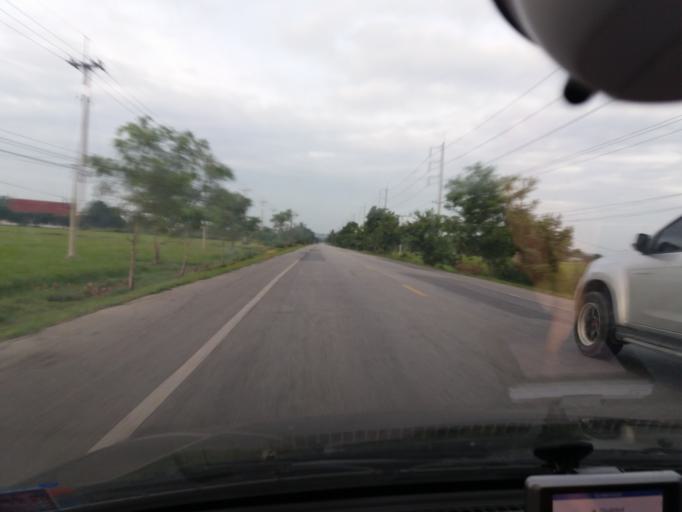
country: TH
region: Suphan Buri
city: U Thong
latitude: 14.4438
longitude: 99.9178
